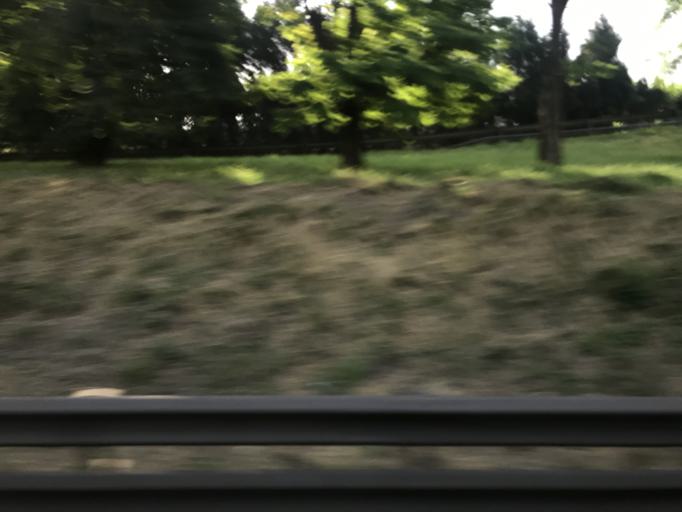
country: ES
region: Basque Country
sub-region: Provincia de Guipuzcoa
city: Olaberria
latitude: 43.0389
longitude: -2.2166
